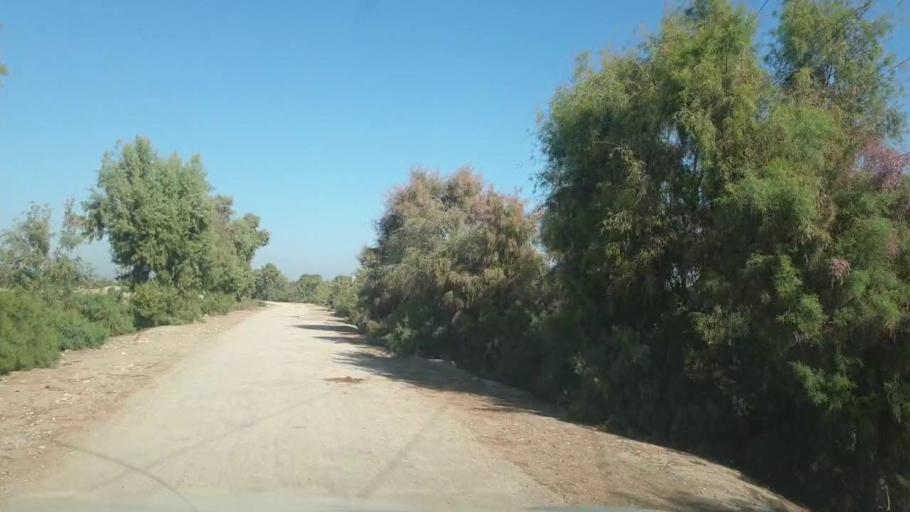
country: PK
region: Sindh
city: Bhan
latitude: 26.5229
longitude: 67.6426
